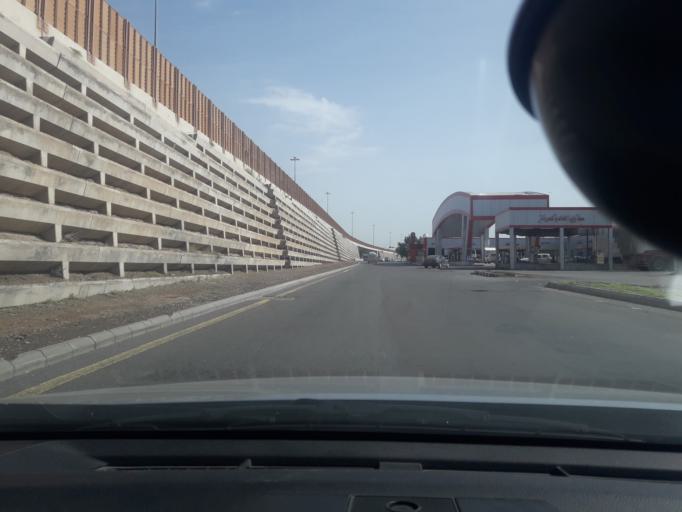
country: SA
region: Al Madinah al Munawwarah
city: Medina
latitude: 24.4502
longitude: 39.6648
